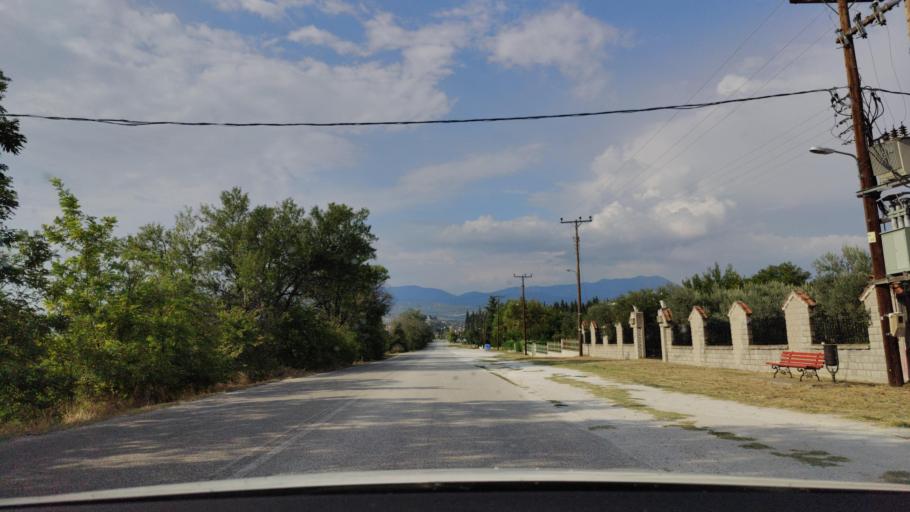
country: GR
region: Central Macedonia
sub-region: Nomos Serron
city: Sidirokastro
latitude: 41.2233
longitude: 23.3903
